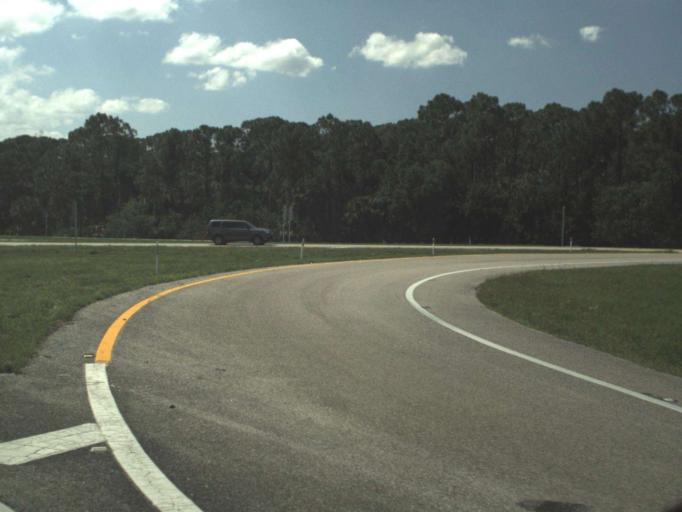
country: US
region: Florida
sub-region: Brevard County
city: Cocoa West
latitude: 28.3600
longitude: -80.8253
